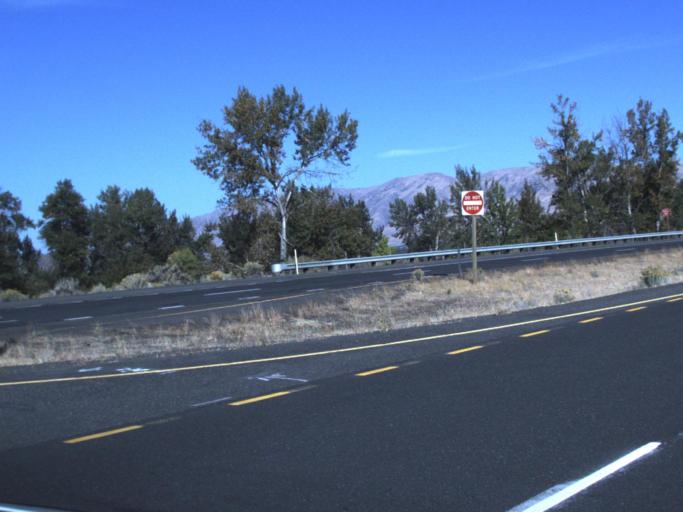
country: US
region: Washington
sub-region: Yakima County
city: Gleed
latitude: 46.6877
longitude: -120.6530
